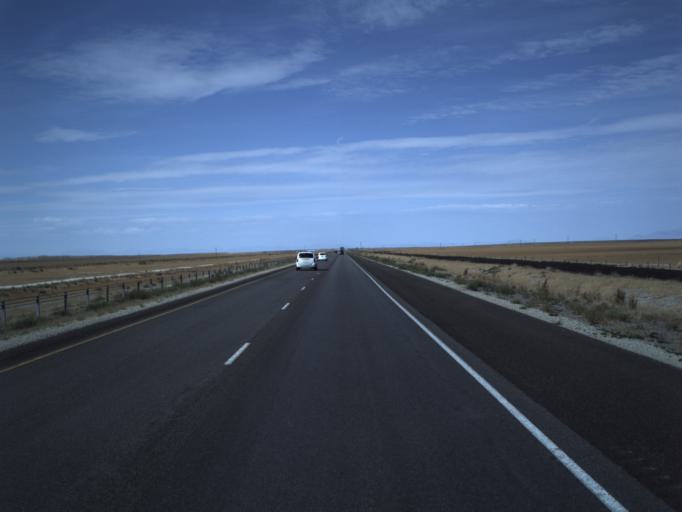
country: US
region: Utah
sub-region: Tooele County
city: Grantsville
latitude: 40.7269
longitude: -113.2226
